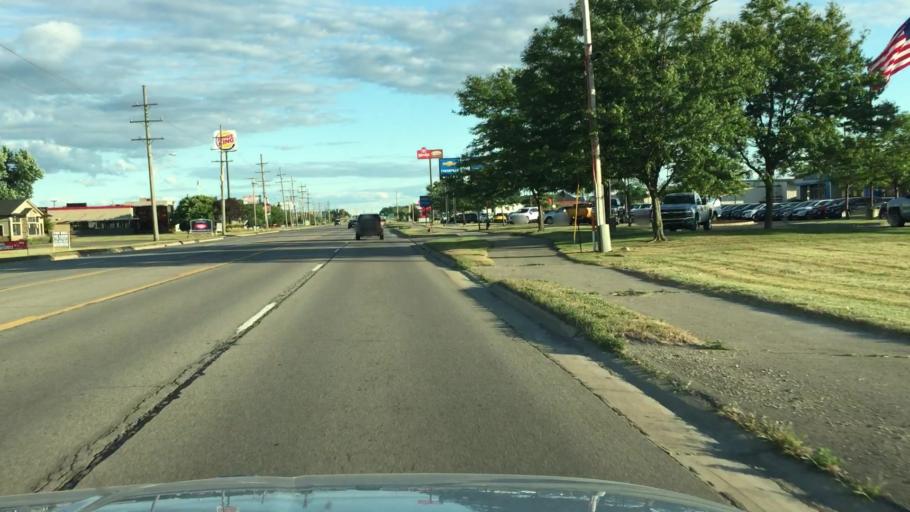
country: US
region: Michigan
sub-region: Lapeer County
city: Imlay City
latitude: 43.0107
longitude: -83.0718
